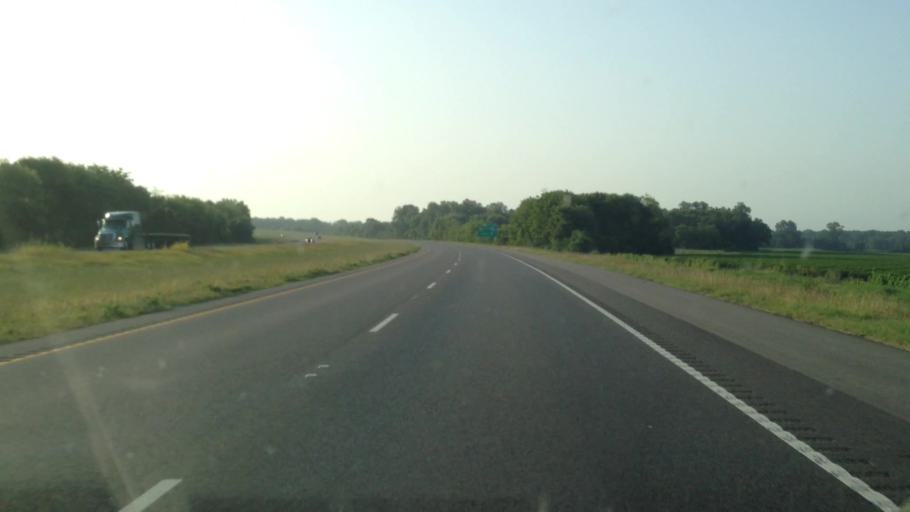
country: US
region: Louisiana
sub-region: Rapides Parish
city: Boyce
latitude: 31.3831
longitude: -92.6798
